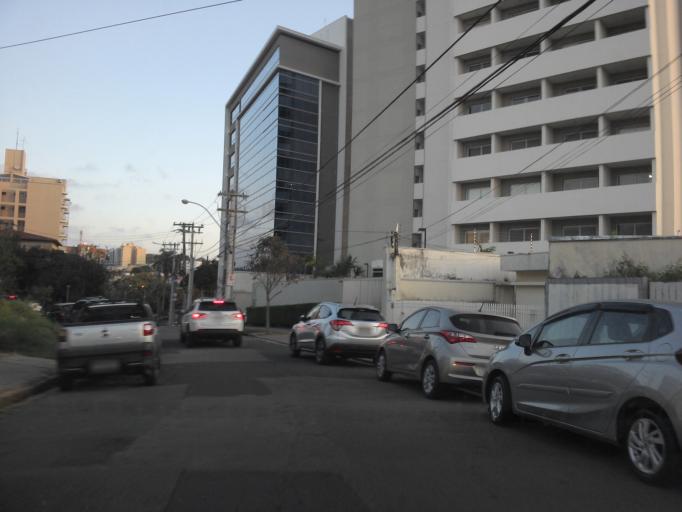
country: BR
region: Sao Paulo
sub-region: Campinas
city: Campinas
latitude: -22.8880
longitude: -47.0436
